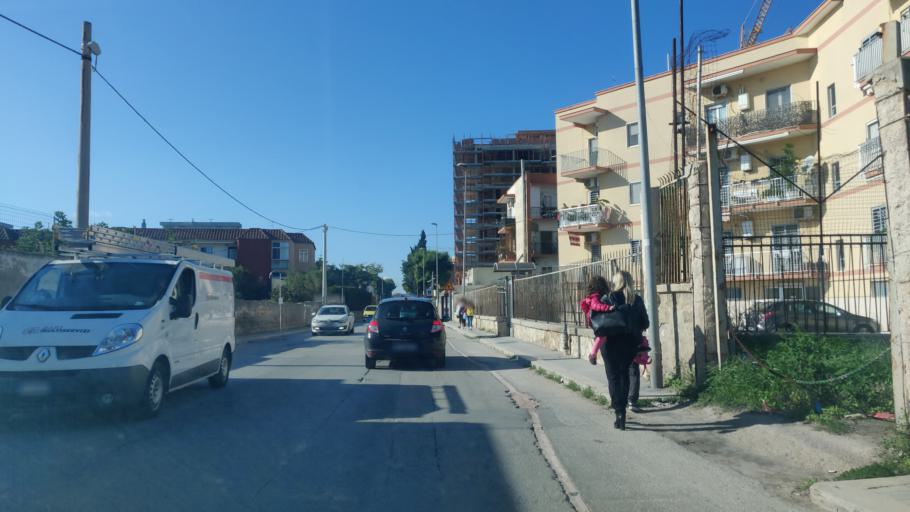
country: IT
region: Apulia
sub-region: Provincia di Bari
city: San Paolo
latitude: 41.1359
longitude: 16.8231
